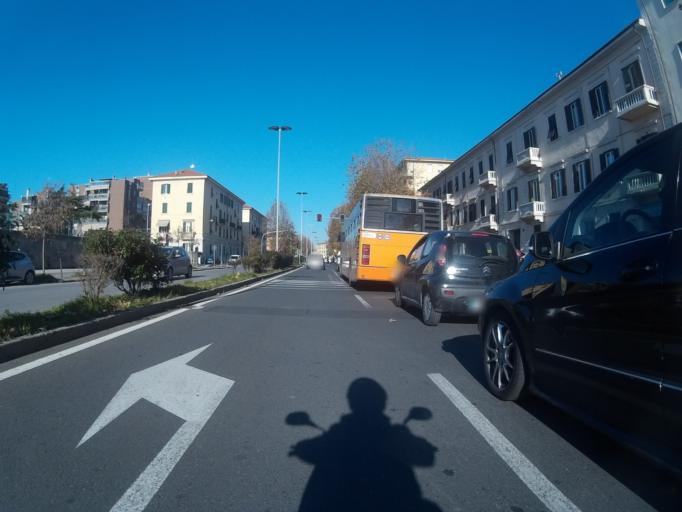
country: IT
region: Tuscany
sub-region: Provincia di Livorno
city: Livorno
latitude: 43.5555
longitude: 10.3272
